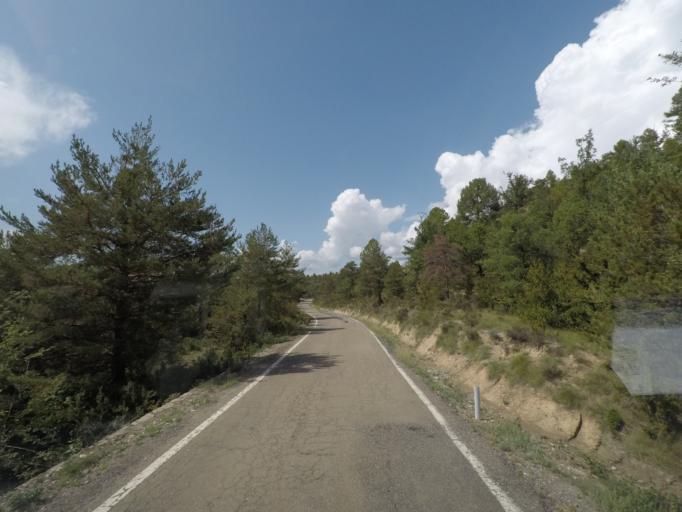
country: ES
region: Aragon
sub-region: Provincia de Huesca
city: Yebra de Basa
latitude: 42.4013
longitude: -0.3567
